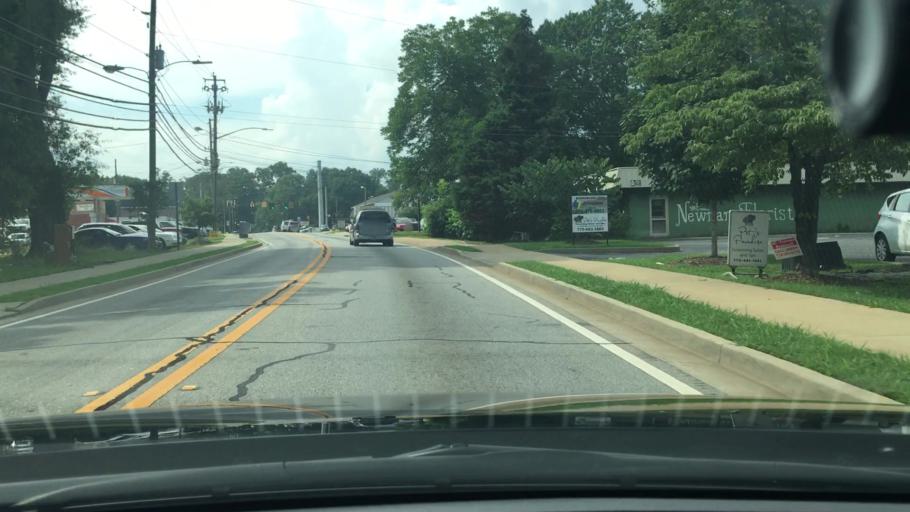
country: US
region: Georgia
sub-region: Coweta County
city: Newnan
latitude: 33.3621
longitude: -84.7929
